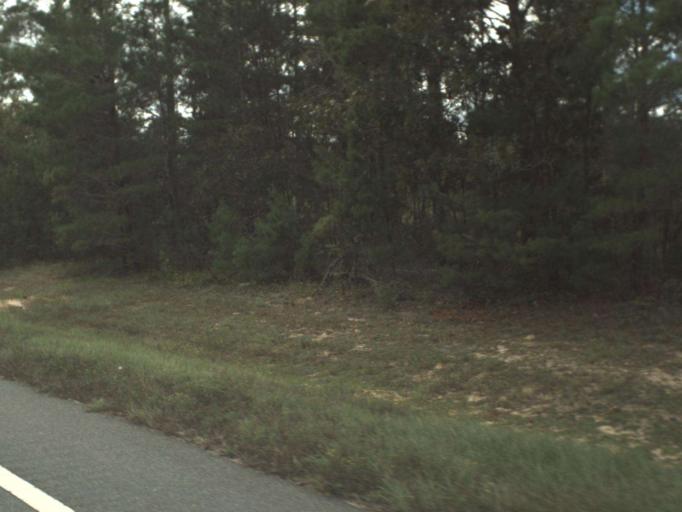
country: US
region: Florida
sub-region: Calhoun County
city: Blountstown
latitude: 30.3830
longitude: -85.2149
